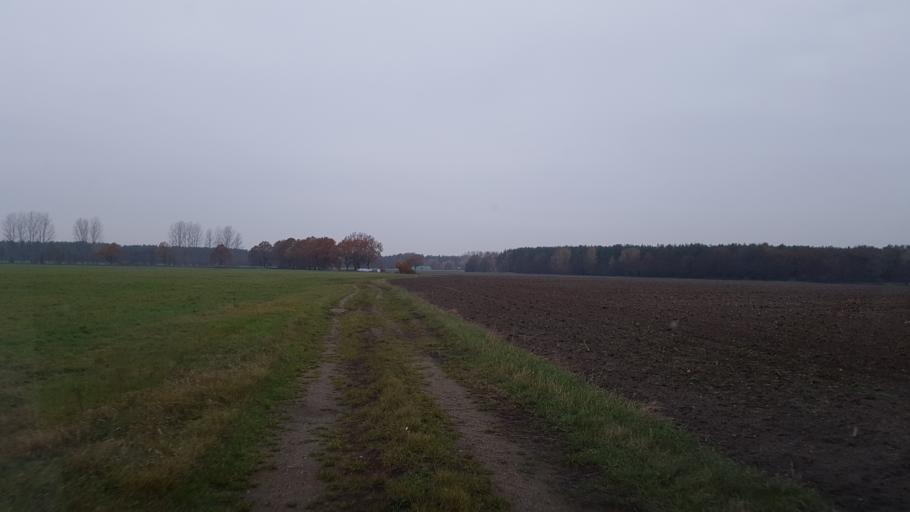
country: DE
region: Brandenburg
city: Schilda
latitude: 51.6214
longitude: 13.3350
